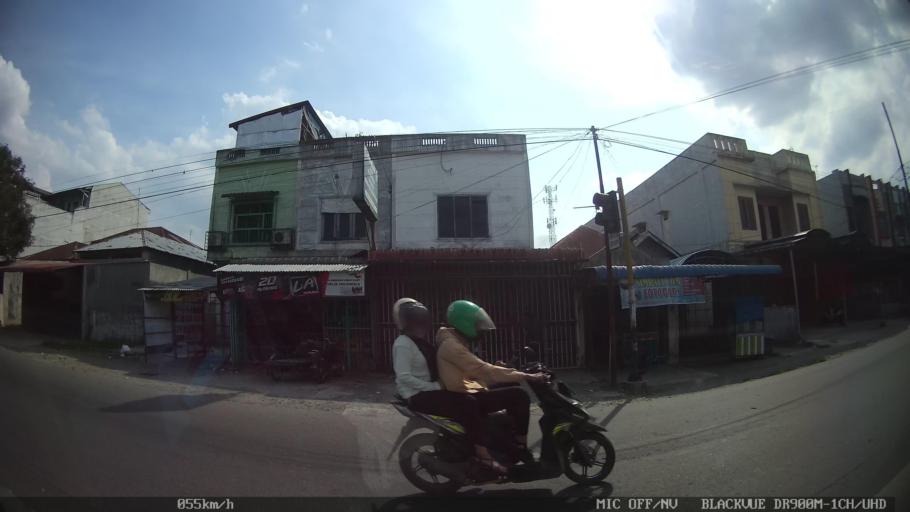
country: ID
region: North Sumatra
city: Binjai
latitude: 3.6321
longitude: 98.4906
